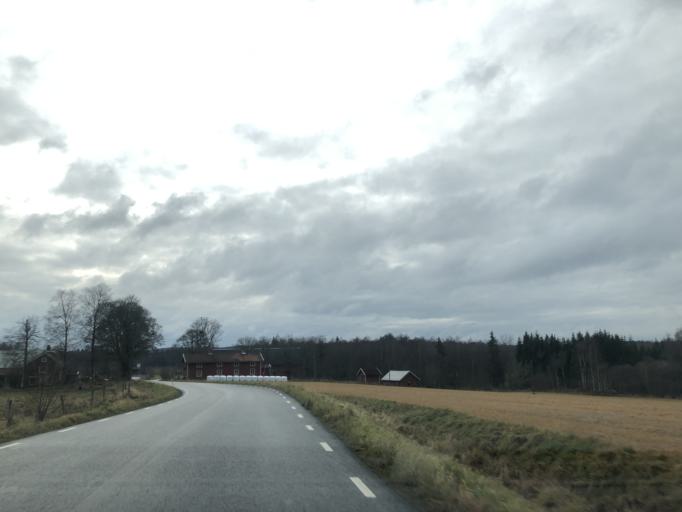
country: SE
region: Vaestra Goetaland
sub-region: Ulricehamns Kommun
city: Ulricehamn
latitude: 57.8135
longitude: 13.2434
